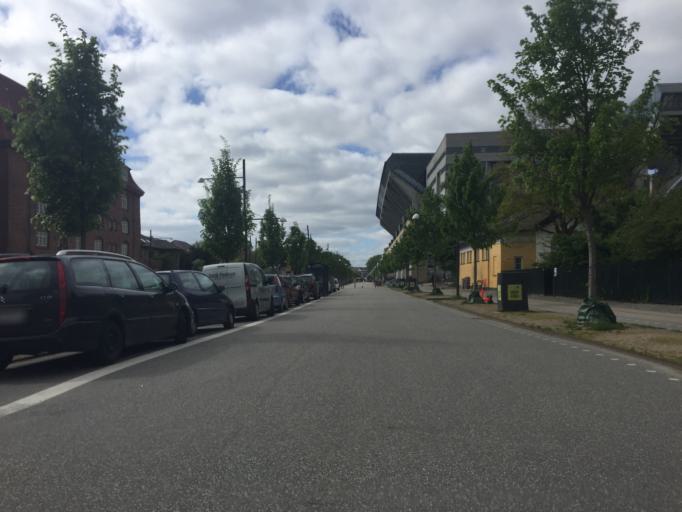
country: DK
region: Capital Region
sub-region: Kobenhavn
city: Copenhagen
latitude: 55.7008
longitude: 12.5737
